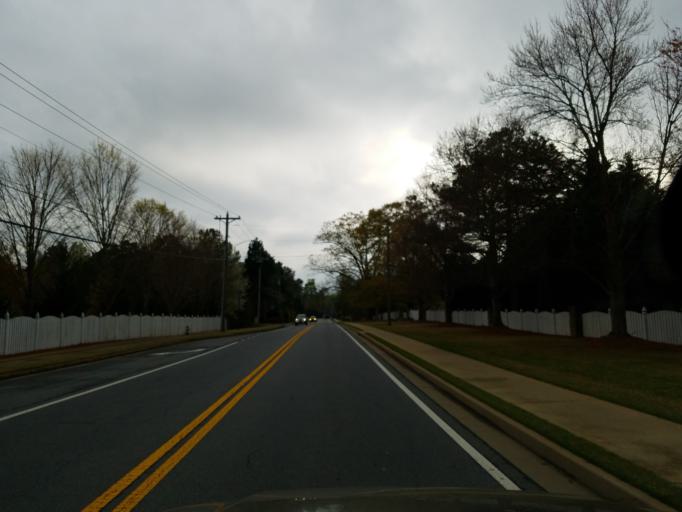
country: US
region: Georgia
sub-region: Fulton County
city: Roswell
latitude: 34.0136
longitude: -84.4436
